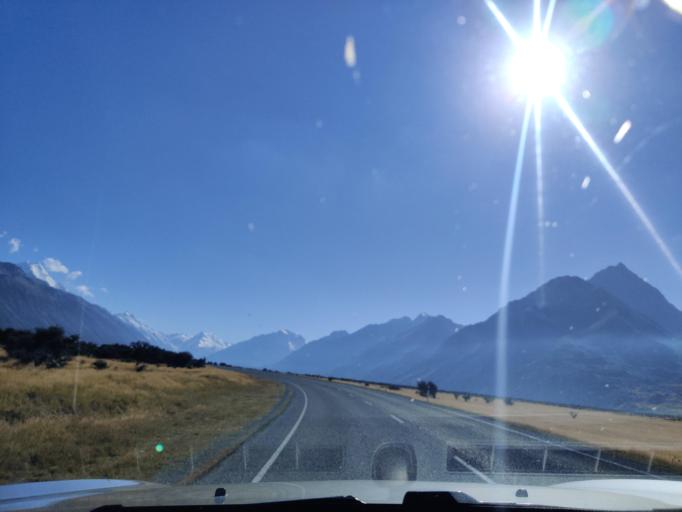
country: NZ
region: Canterbury
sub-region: Timaru District
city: Pleasant Point
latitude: -43.7835
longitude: 170.1231
